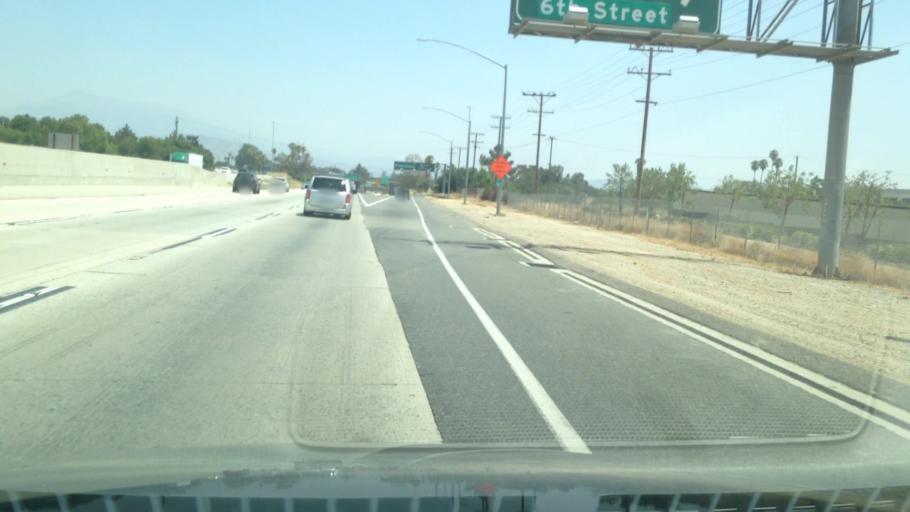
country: US
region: California
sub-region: Riverside County
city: Beaumont
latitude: 33.9362
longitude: -116.9951
